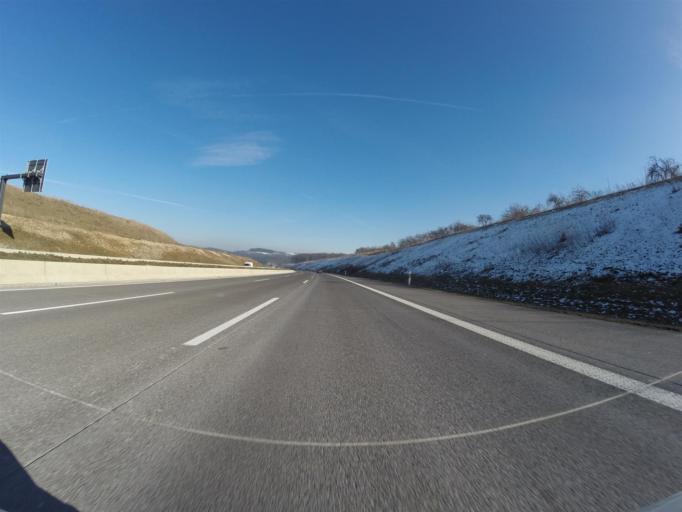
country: DE
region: Thuringia
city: Bucha
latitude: 50.8752
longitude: 11.5168
